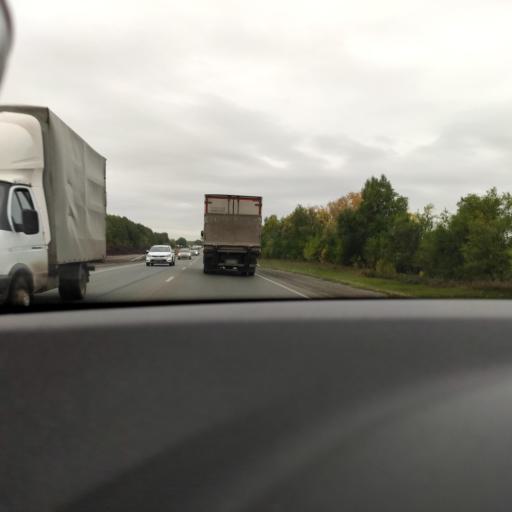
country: RU
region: Samara
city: Krasnyy Yar
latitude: 53.4464
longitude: 50.3800
